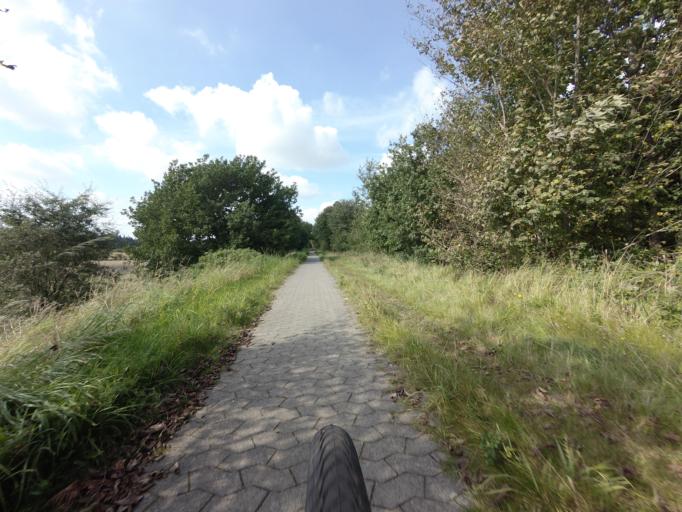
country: DK
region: Central Jutland
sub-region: Viborg Kommune
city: Viborg
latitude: 56.3970
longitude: 9.3293
